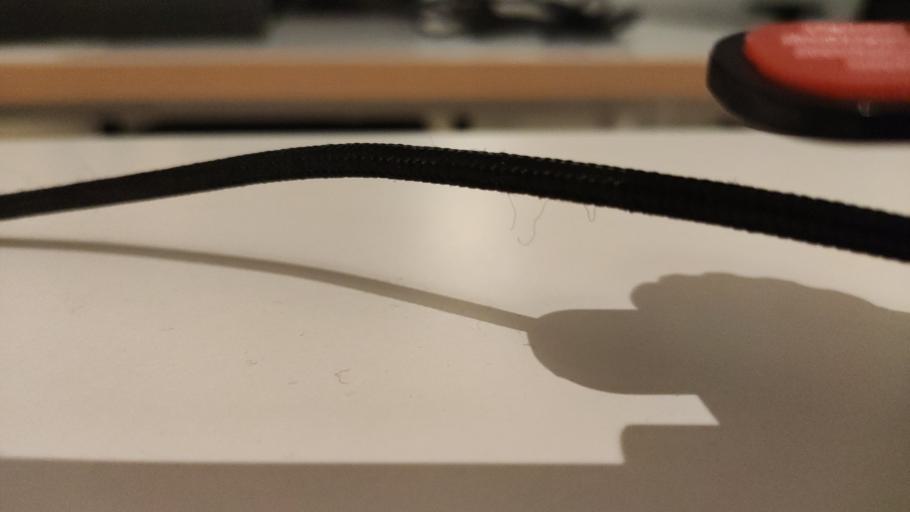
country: RU
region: Moskovskaya
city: Novoye
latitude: 55.6229
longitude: 38.9461
